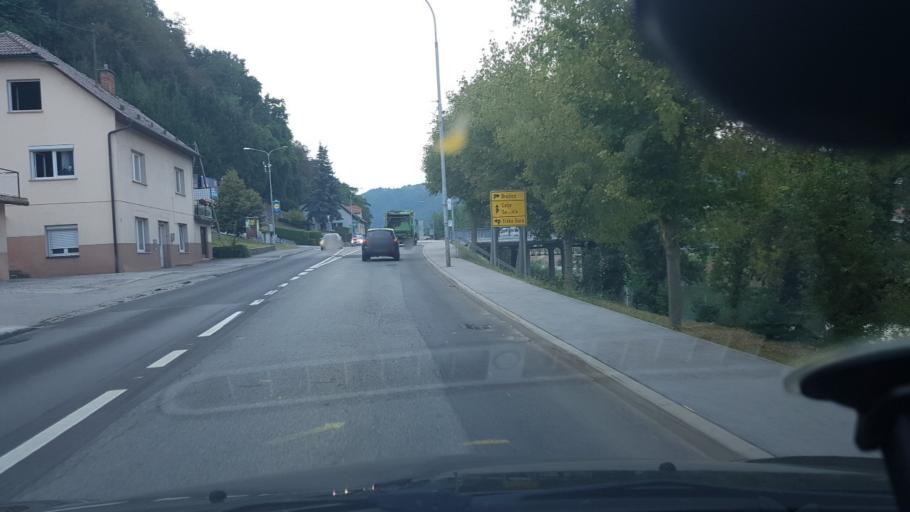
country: SI
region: Krsko
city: Krsko
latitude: 45.9558
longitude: 15.4864
